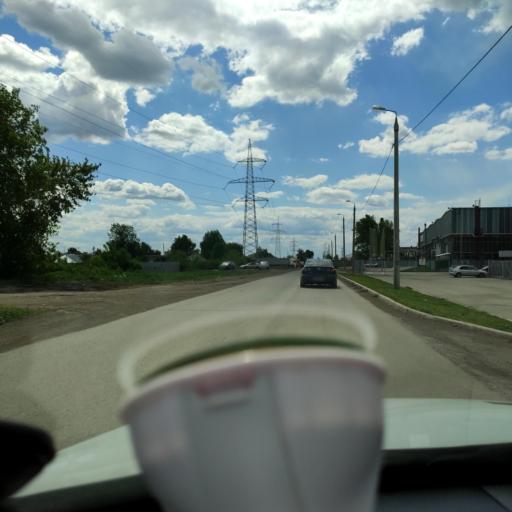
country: RU
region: Samara
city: Petra-Dubrava
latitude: 53.2639
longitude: 50.3170
